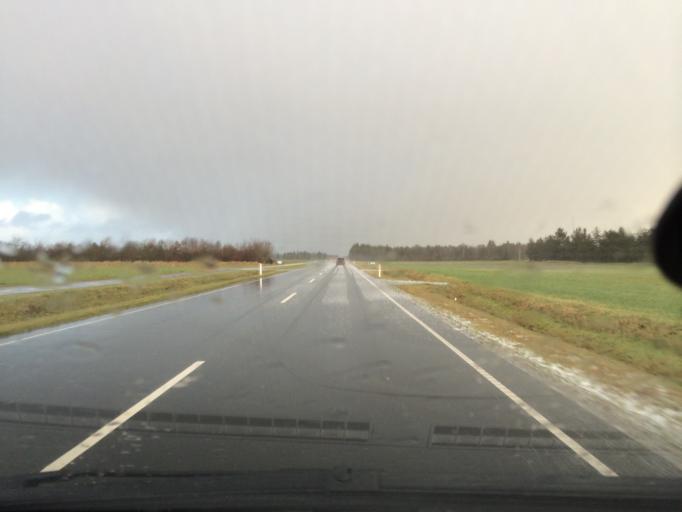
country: DK
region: Central Jutland
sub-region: Holstebro Kommune
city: Ulfborg
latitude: 56.2677
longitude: 8.2648
